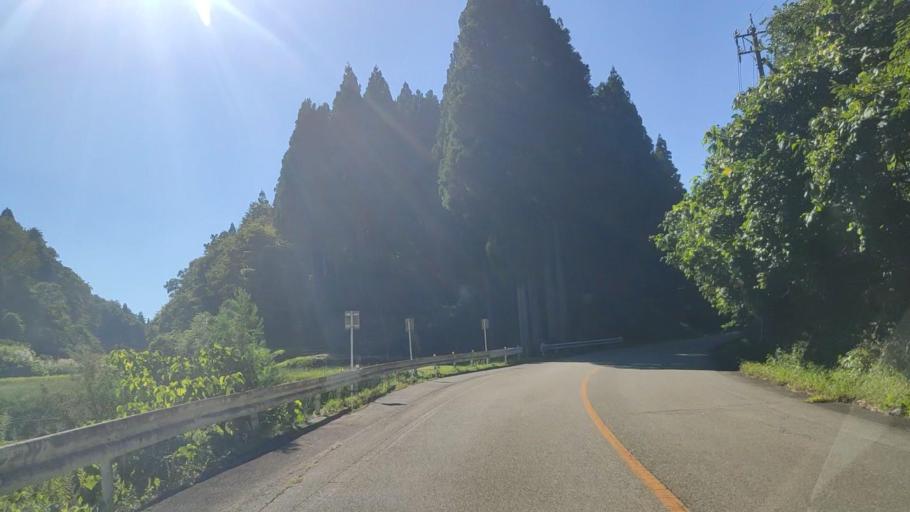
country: JP
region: Ishikawa
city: Nanao
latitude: 37.3211
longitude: 137.1760
